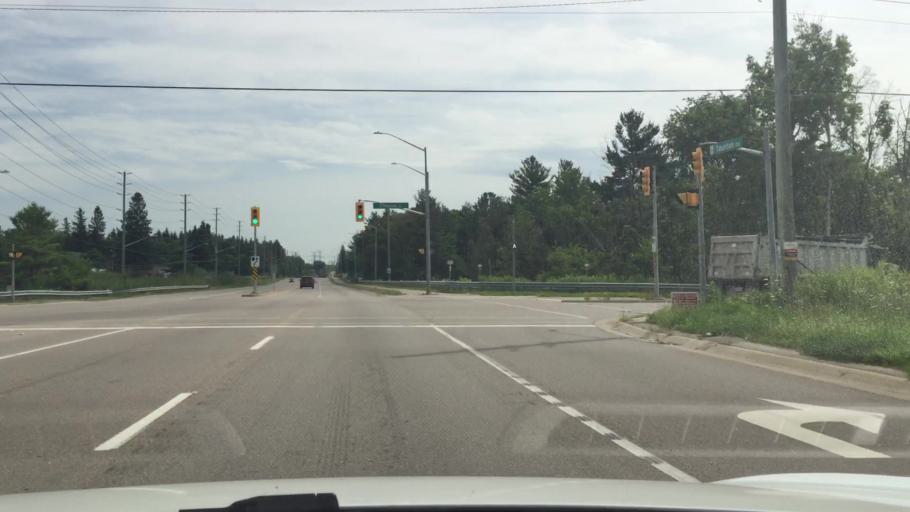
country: CA
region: Ontario
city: Ajax
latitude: 43.8885
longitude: -79.0705
